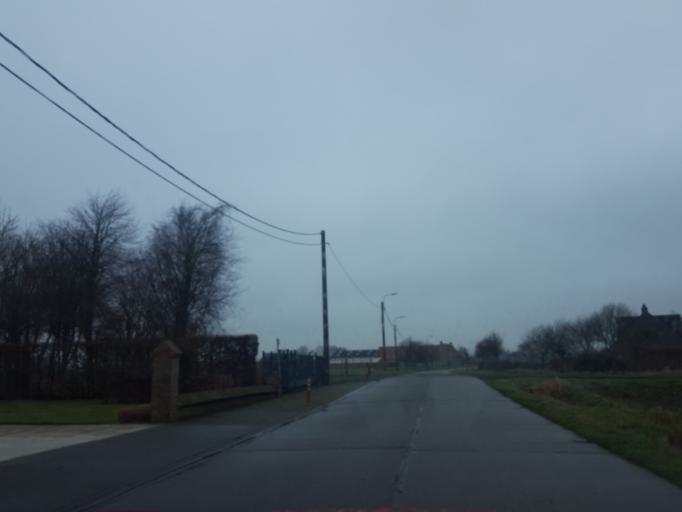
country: BE
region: Flanders
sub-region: Provincie West-Vlaanderen
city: Ieper
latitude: 50.8860
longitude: 2.8578
